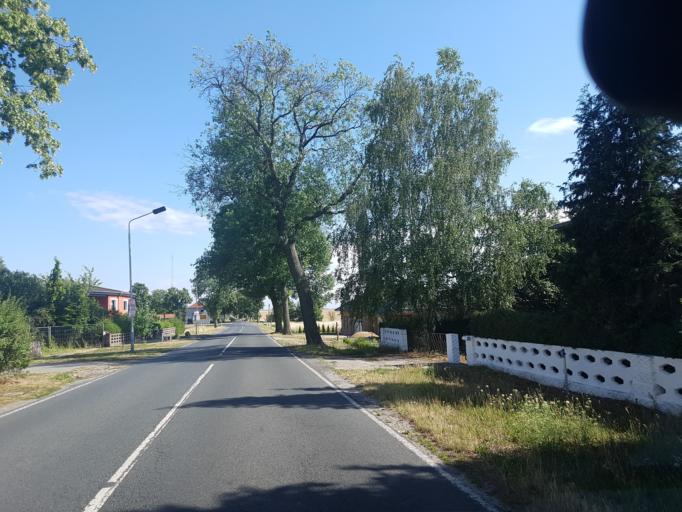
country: DE
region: Brandenburg
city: Juterbog
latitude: 51.9805
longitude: 13.1012
